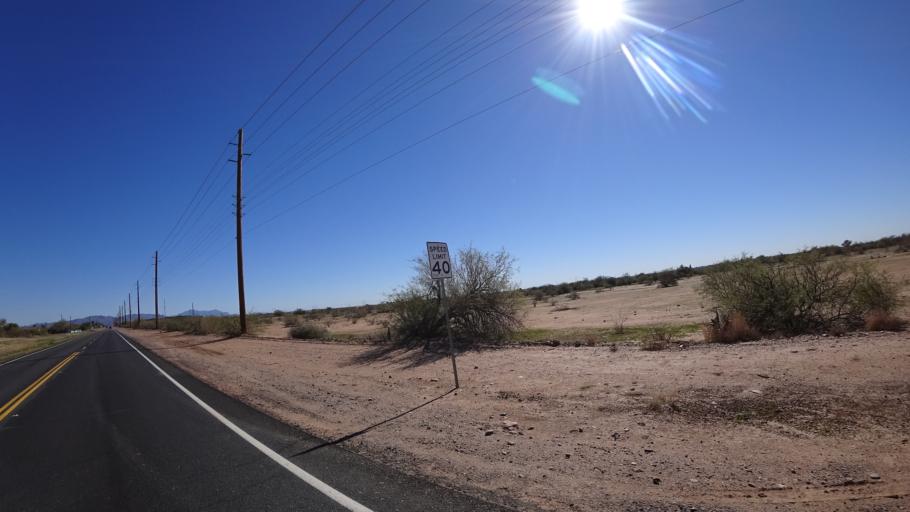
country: US
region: Arizona
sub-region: Maricopa County
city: Scottsdale
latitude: 33.4952
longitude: -111.8375
